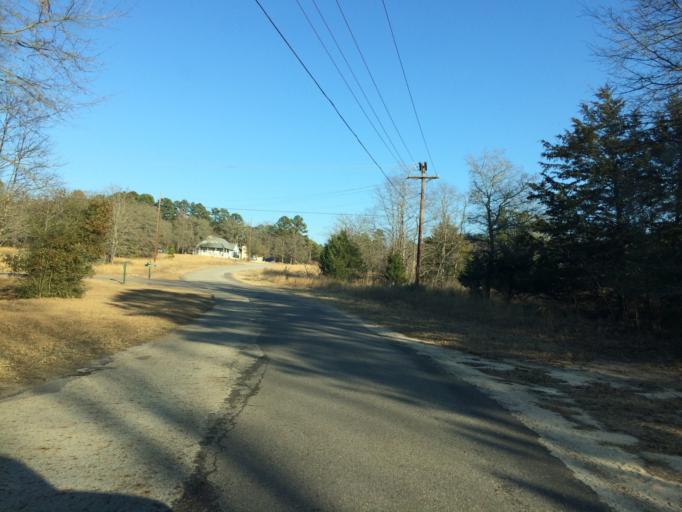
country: US
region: Texas
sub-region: Wood County
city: Hawkins
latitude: 32.7203
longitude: -95.1749
